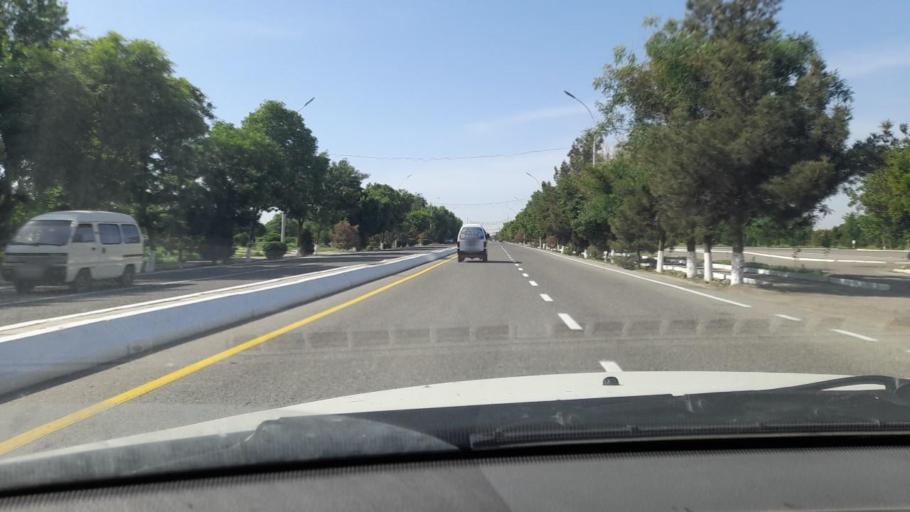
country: UZ
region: Bukhara
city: Bukhara
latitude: 39.7979
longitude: 64.4355
